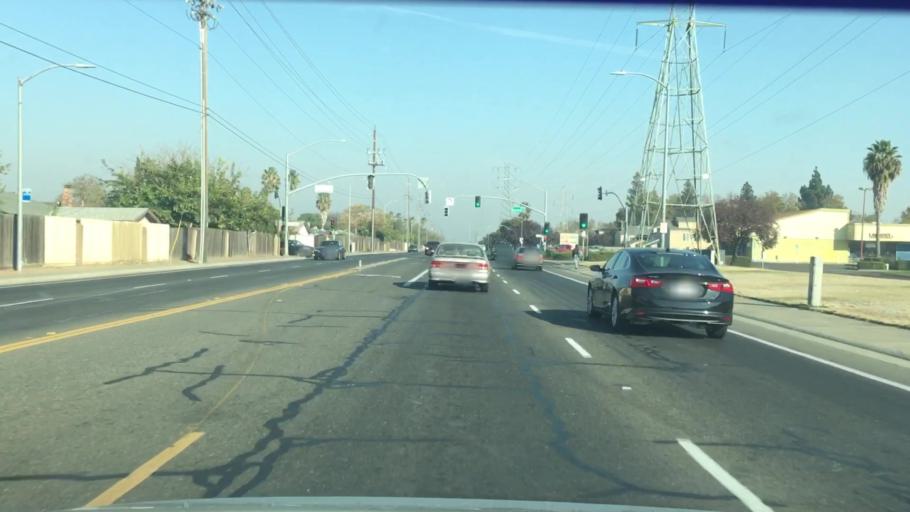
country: US
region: California
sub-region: Sacramento County
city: Florin
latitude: 38.4872
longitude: -121.4088
